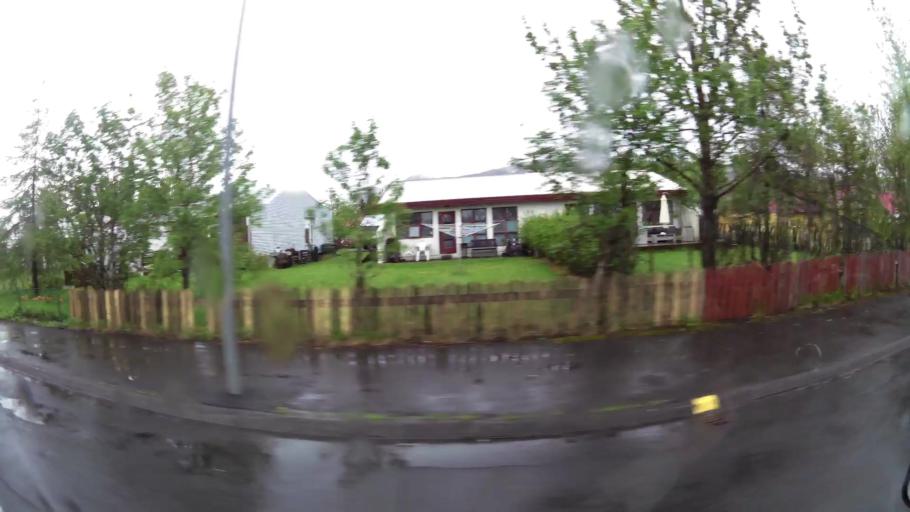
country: IS
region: South
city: Hveragerdi
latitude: 64.0002
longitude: -21.1945
